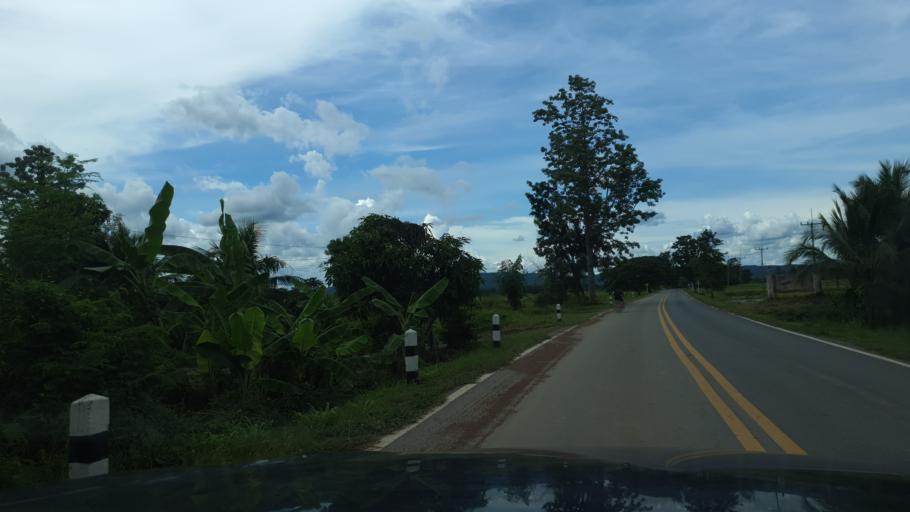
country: TH
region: Sukhothai
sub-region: Amphoe Si Satchanalai
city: Si Satchanalai
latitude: 17.4664
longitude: 99.7575
